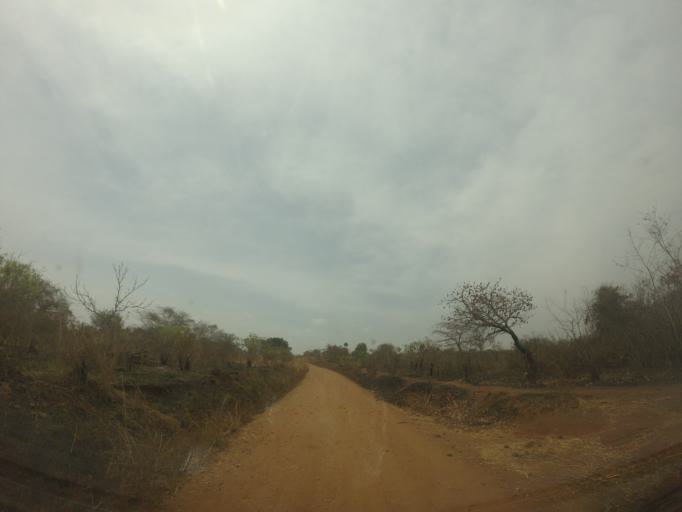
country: UG
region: Northern Region
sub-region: Nebbi District
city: Nebbi
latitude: 2.6317
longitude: 31.0356
